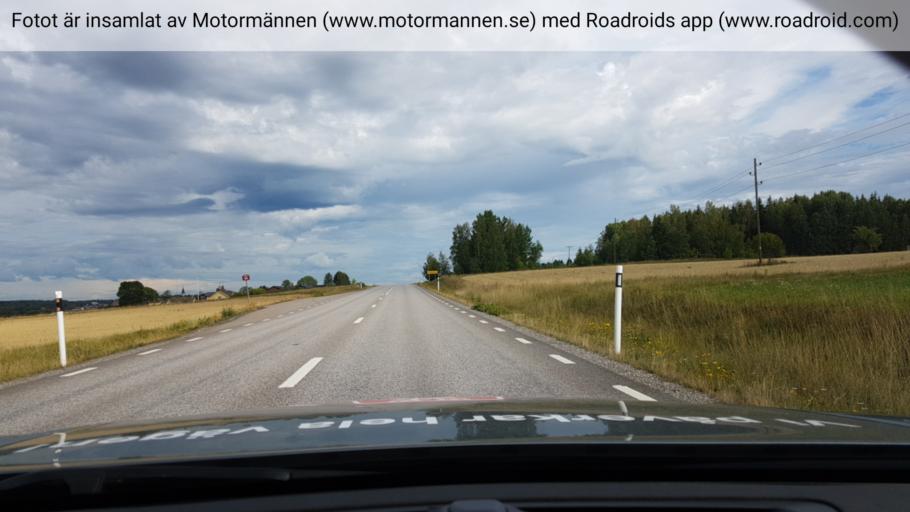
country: SE
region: Uppsala
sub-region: Heby Kommun
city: Heby
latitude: 59.9215
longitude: 16.8817
